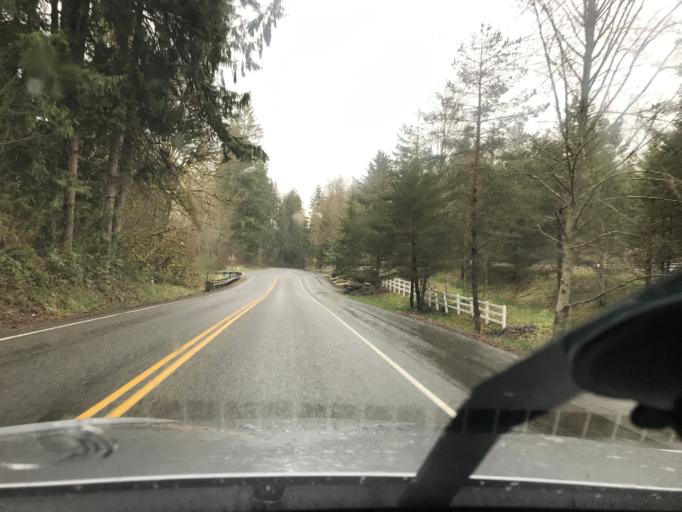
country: US
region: Washington
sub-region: King County
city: Ames Lake
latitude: 47.6601
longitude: -121.9655
